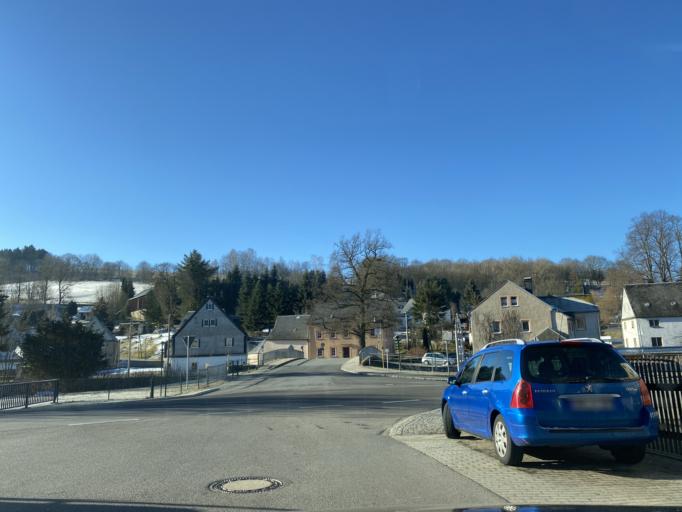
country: DE
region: Saxony
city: Wiesa
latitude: 50.6109
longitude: 13.0203
